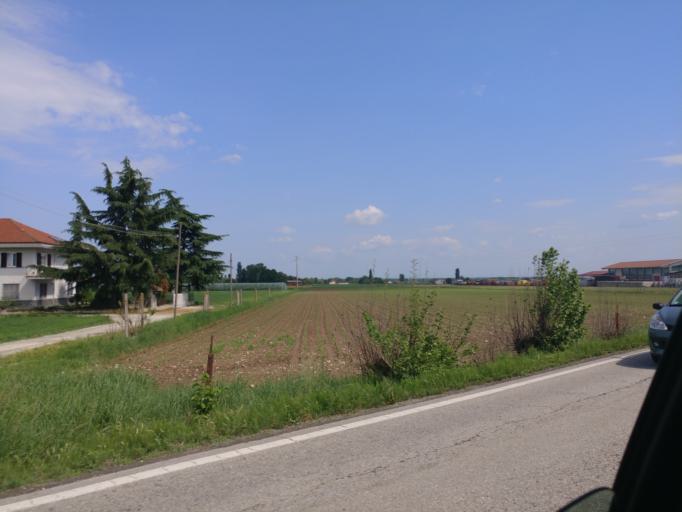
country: IT
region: Piedmont
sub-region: Provincia di Torino
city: Cavour
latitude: 44.7789
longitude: 7.3850
